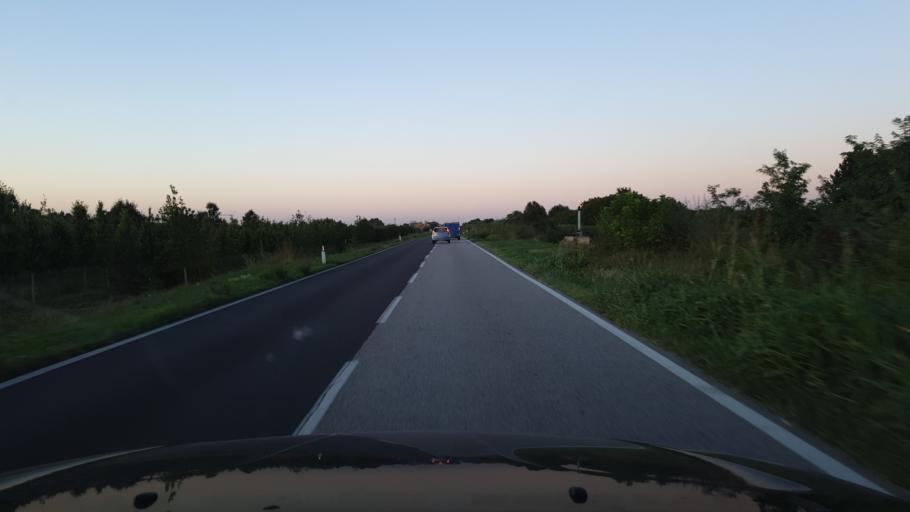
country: IT
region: Emilia-Romagna
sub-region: Provincia di Bologna
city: Ca De Fabbri
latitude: 44.6117
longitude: 11.4480
